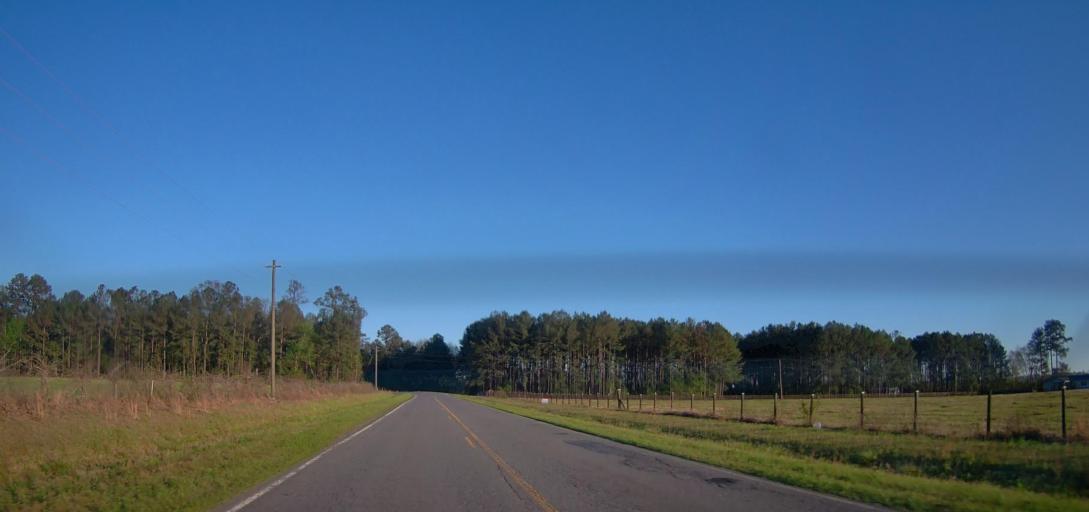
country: US
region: Georgia
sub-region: Wilkinson County
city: Gordon
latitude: 32.8844
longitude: -83.2926
